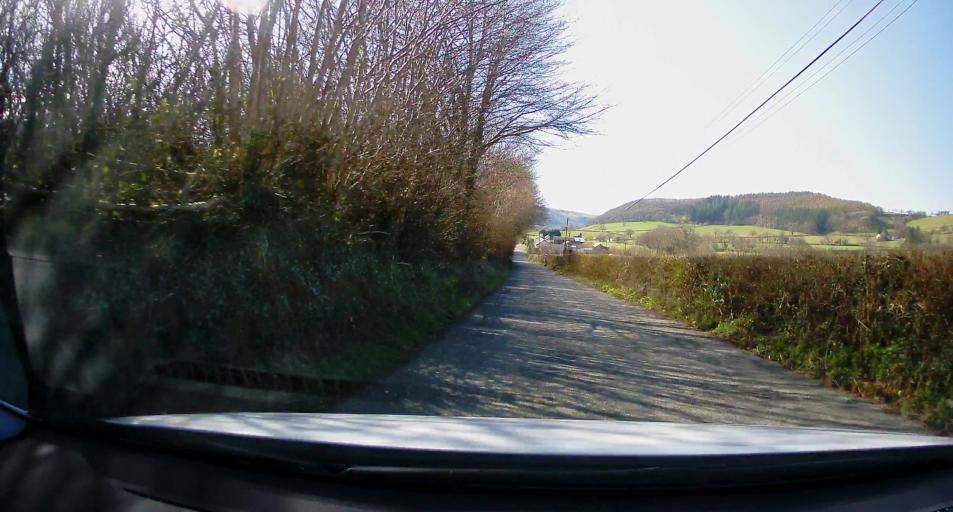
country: GB
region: Wales
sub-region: County of Ceredigion
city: Lledrod
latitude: 52.3531
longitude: -3.9402
